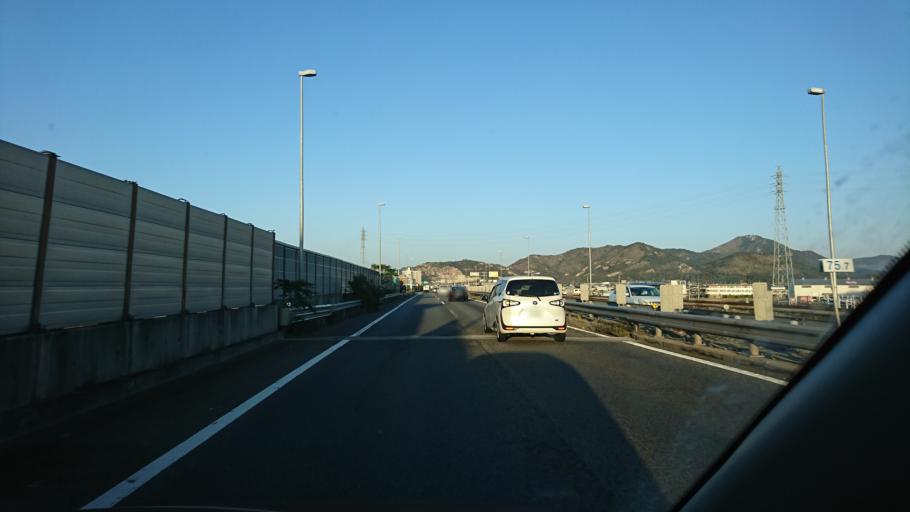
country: JP
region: Hyogo
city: Kakogawacho-honmachi
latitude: 34.7874
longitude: 134.8198
